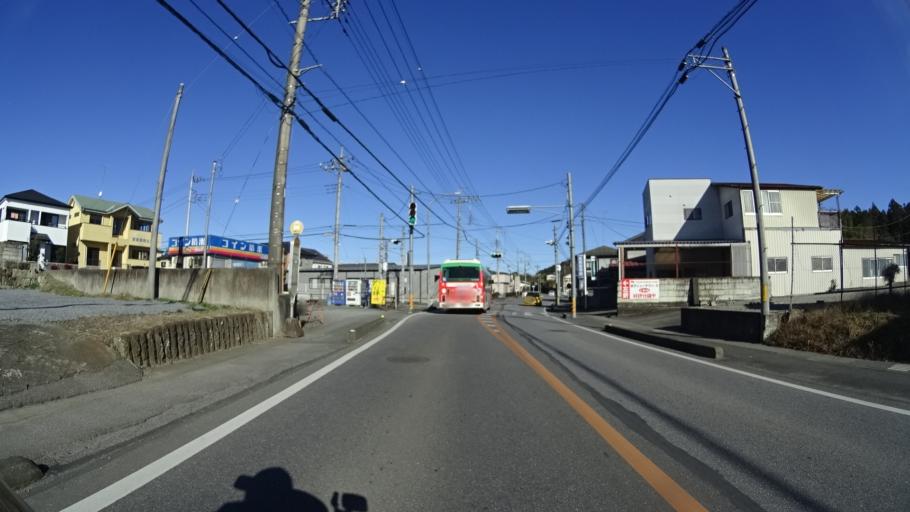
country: JP
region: Tochigi
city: Kanuma
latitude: 36.5791
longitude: 139.7654
